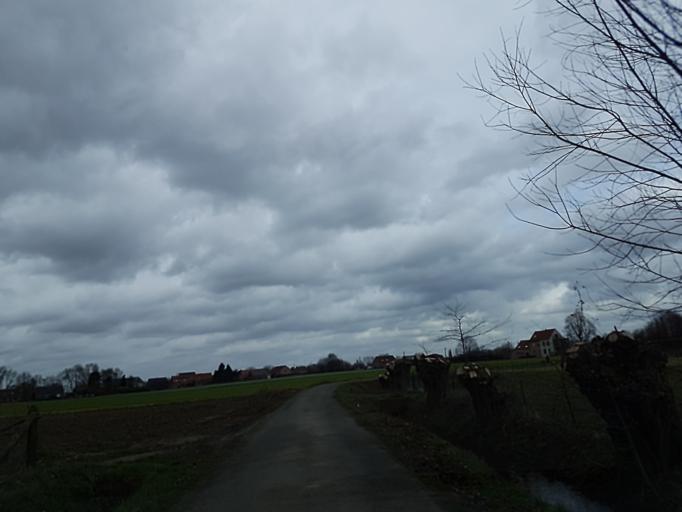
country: BE
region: Flanders
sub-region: Provincie Vlaams-Brabant
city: Zemst
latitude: 50.9953
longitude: 4.4267
